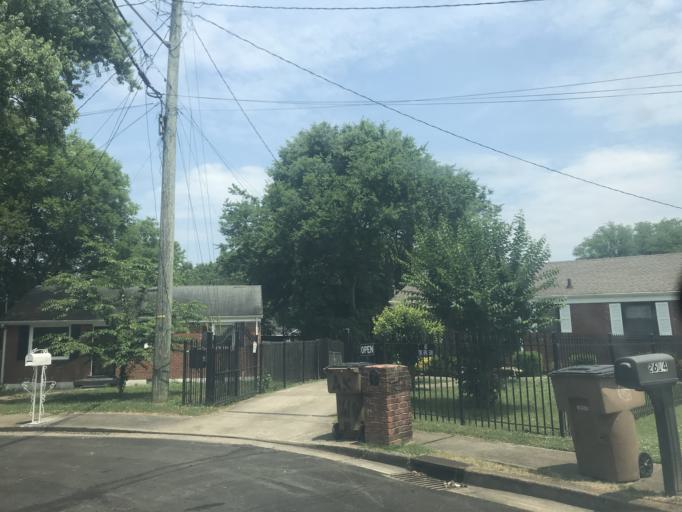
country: US
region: Tennessee
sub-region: Davidson County
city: Nashville
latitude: 36.1819
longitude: -86.8206
